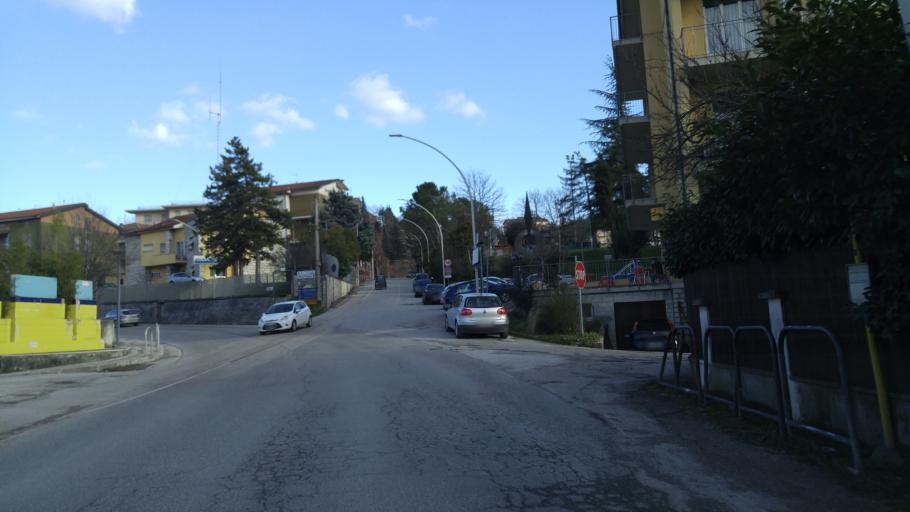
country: IT
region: The Marches
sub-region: Provincia di Pesaro e Urbino
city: Cagli
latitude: 43.5453
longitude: 12.6521
